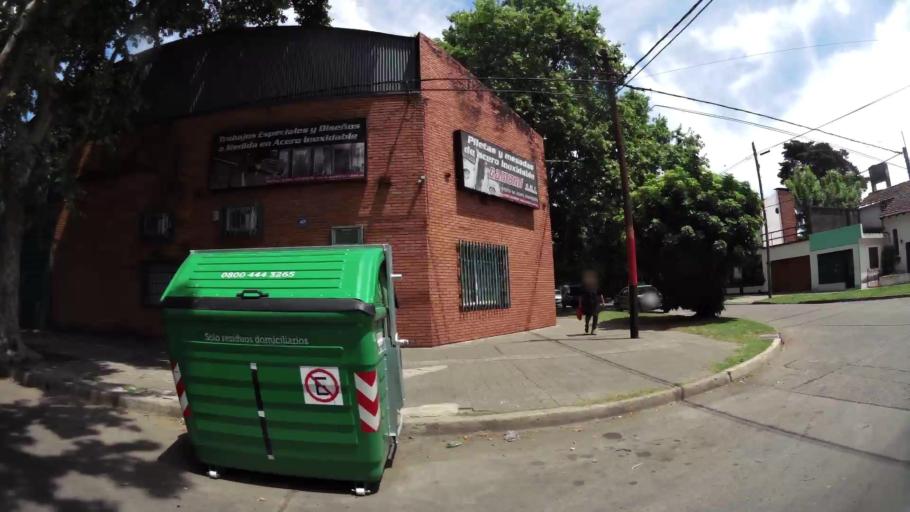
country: AR
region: Santa Fe
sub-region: Departamento de Rosario
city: Rosario
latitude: -32.9723
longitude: -60.6315
